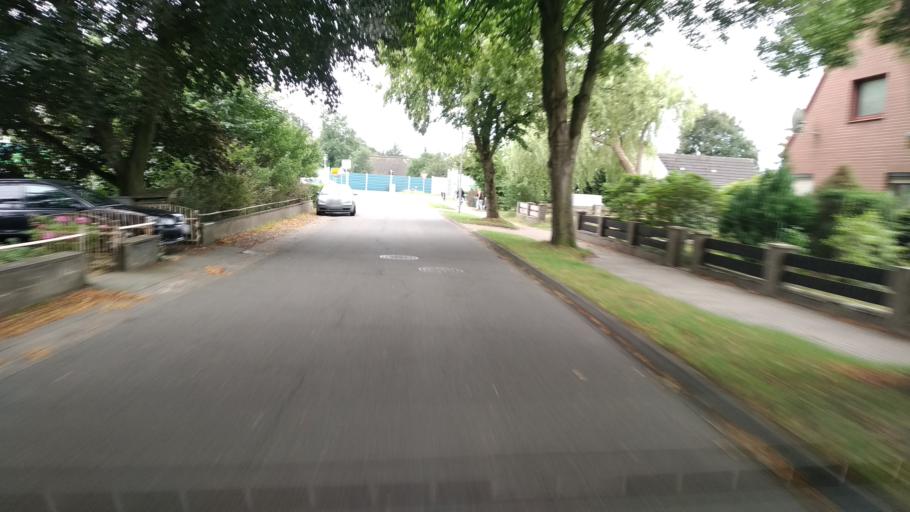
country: DE
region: Schleswig-Holstein
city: Schuby
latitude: 54.5220
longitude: 9.4810
